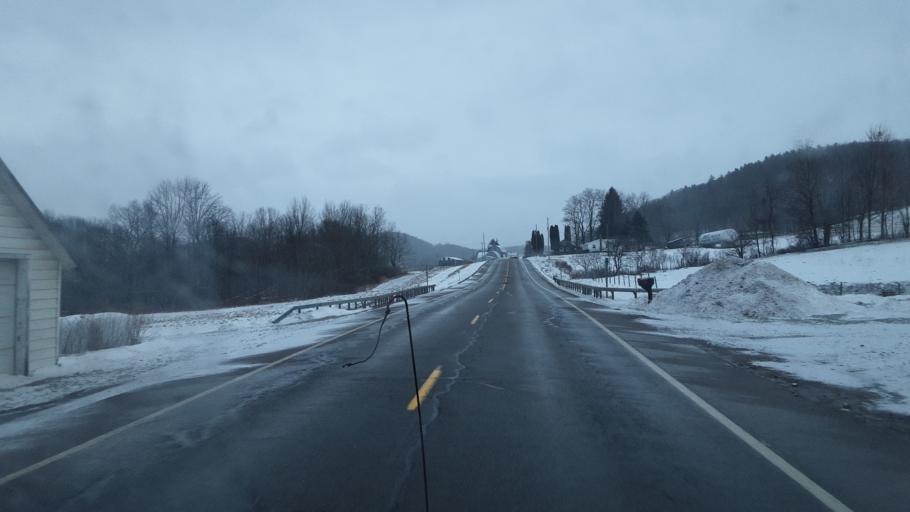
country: US
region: Pennsylvania
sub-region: Tioga County
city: Westfield
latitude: 42.0824
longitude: -77.5416
